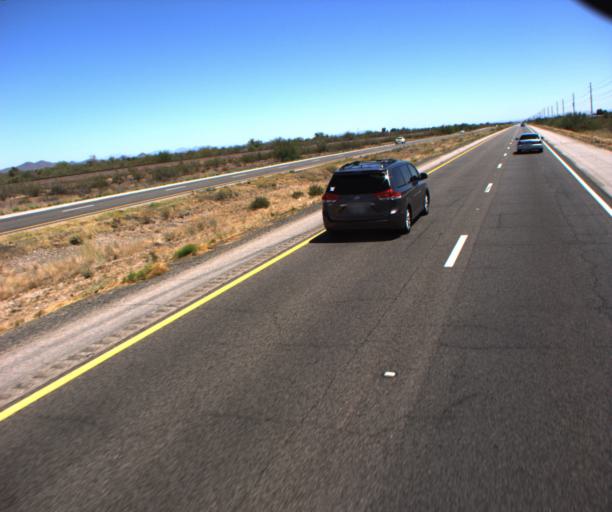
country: US
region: Arizona
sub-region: Maricopa County
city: Sun City West
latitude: 33.7934
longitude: -112.5488
